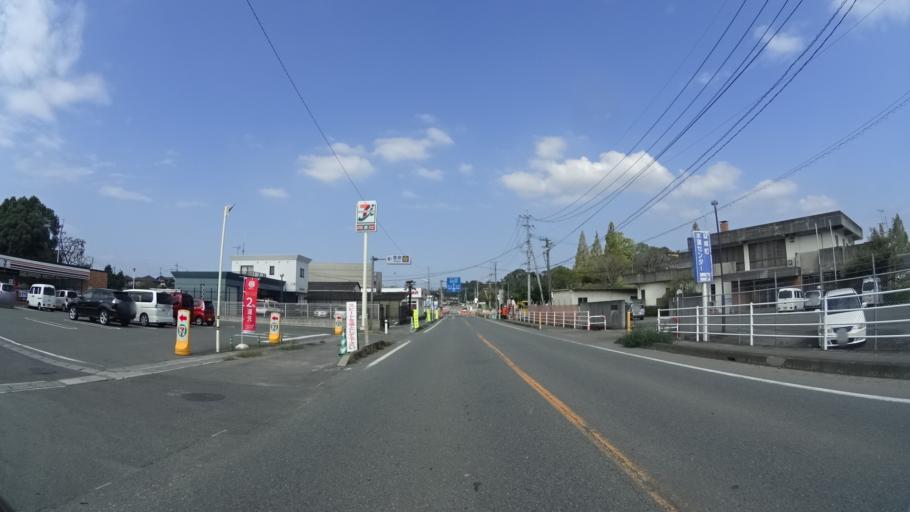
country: JP
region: Kumamoto
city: Ozu
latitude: 32.7871
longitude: 130.8207
